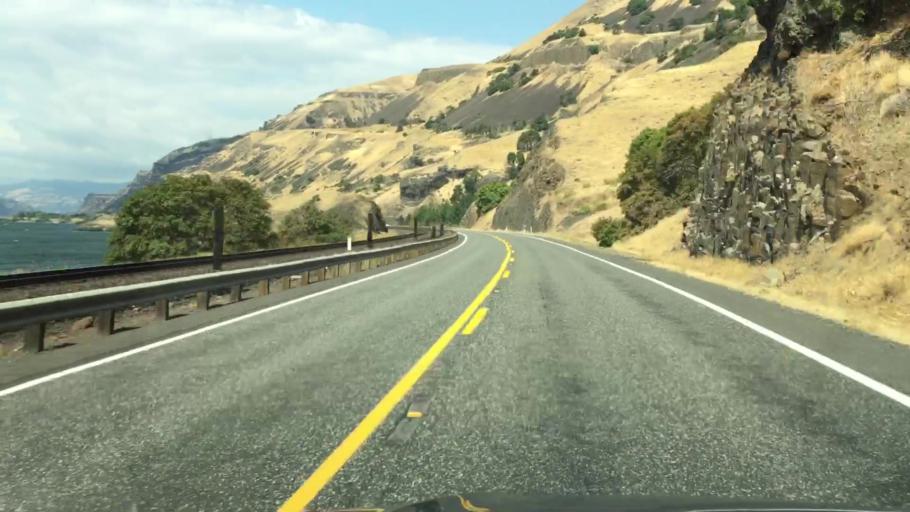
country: US
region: Oregon
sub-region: Wasco County
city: Chenoweth
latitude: 45.6714
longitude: -121.2102
